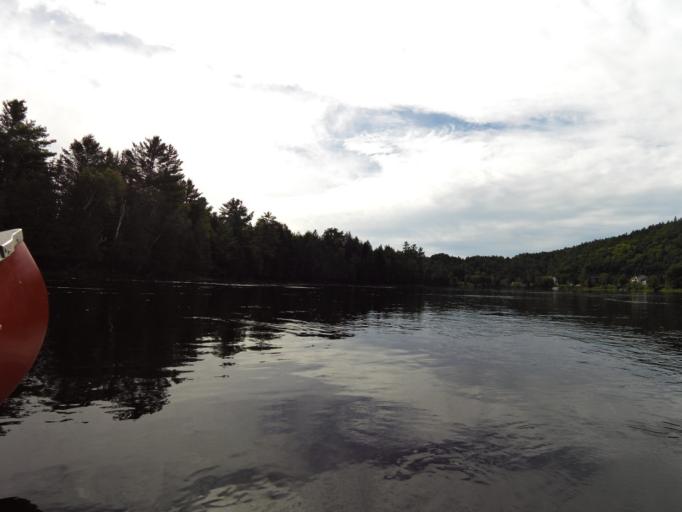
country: CA
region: Quebec
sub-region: Outaouais
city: Wakefield
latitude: 45.7767
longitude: -75.9401
